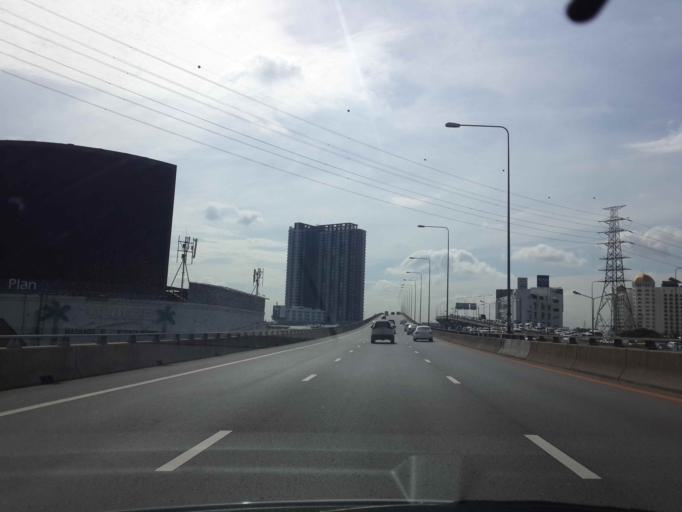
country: TH
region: Bangkok
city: Watthana
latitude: 13.7495
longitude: 100.5998
